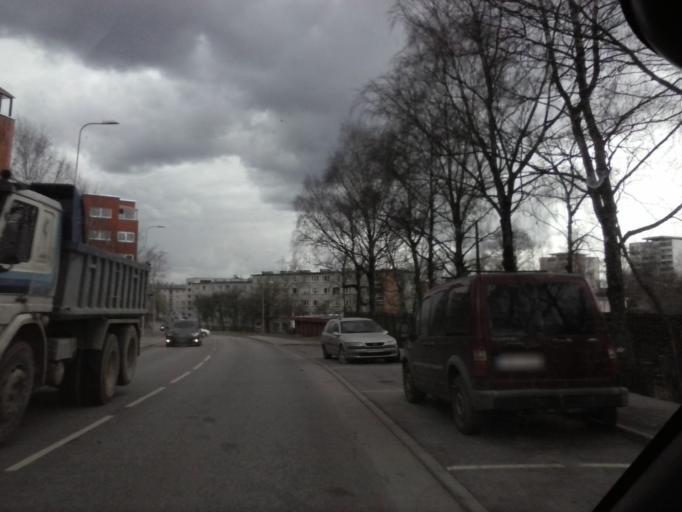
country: EE
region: Harju
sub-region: Tallinna linn
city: Tallinn
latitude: 59.4326
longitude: 24.7954
